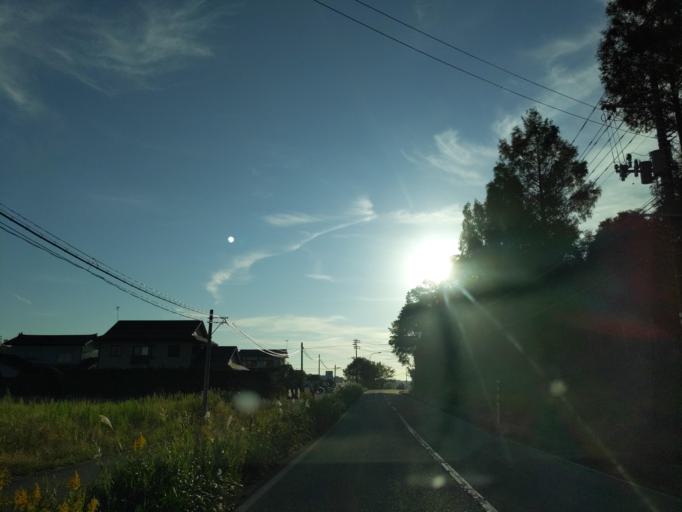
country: JP
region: Niigata
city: Nagaoka
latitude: 37.5786
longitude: 138.7615
